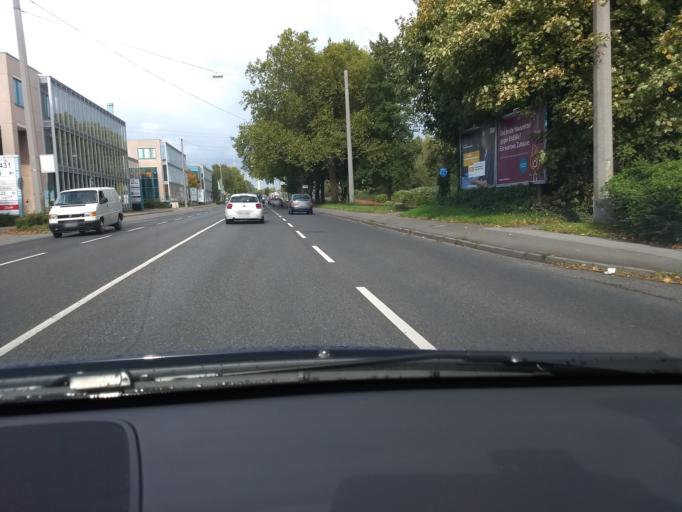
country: DE
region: North Rhine-Westphalia
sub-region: Regierungsbezirk Dusseldorf
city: Essen
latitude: 51.4900
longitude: 6.9982
